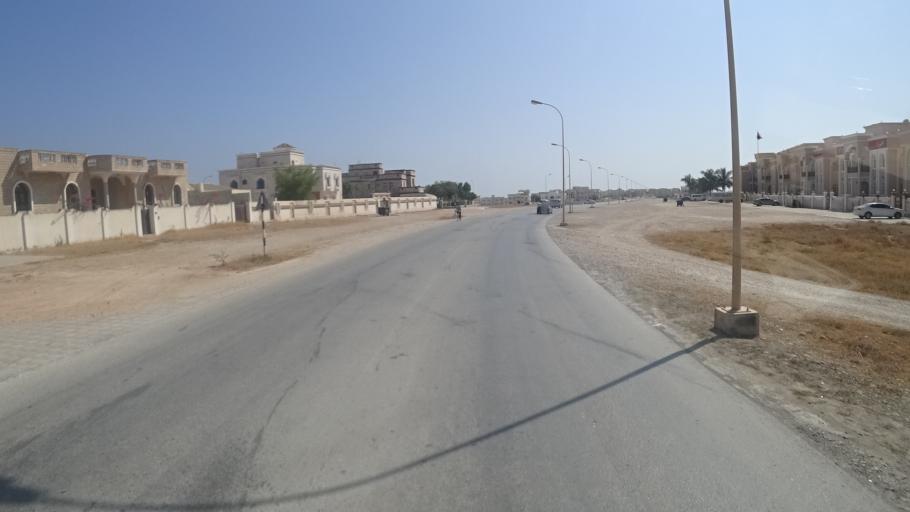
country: OM
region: Zufar
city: Salalah
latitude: 17.0096
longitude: 54.0263
